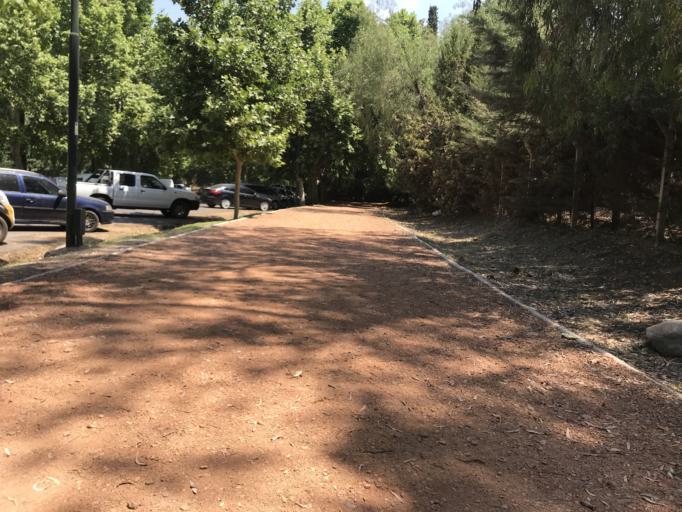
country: AR
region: Mendoza
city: Mendoza
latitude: -32.8970
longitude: -68.8678
